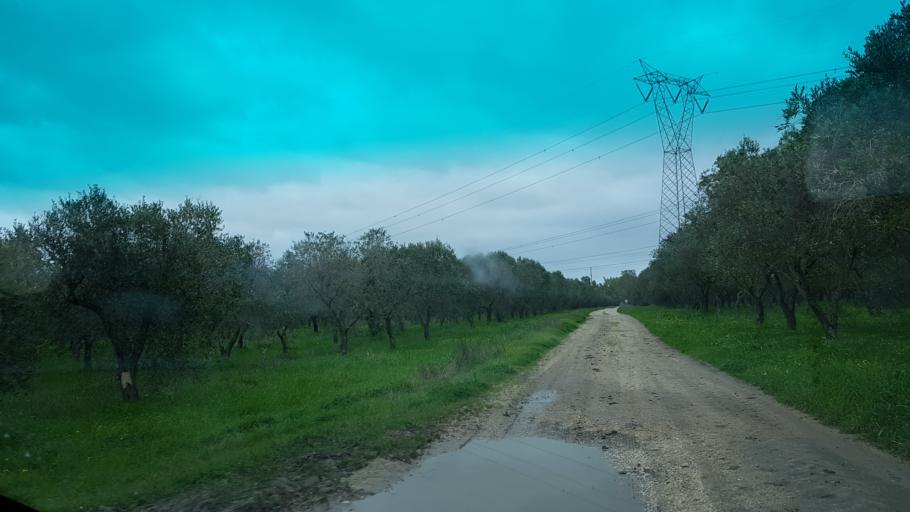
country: IT
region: Apulia
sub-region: Provincia di Brindisi
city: Tuturano
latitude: 40.5604
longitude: 17.9985
